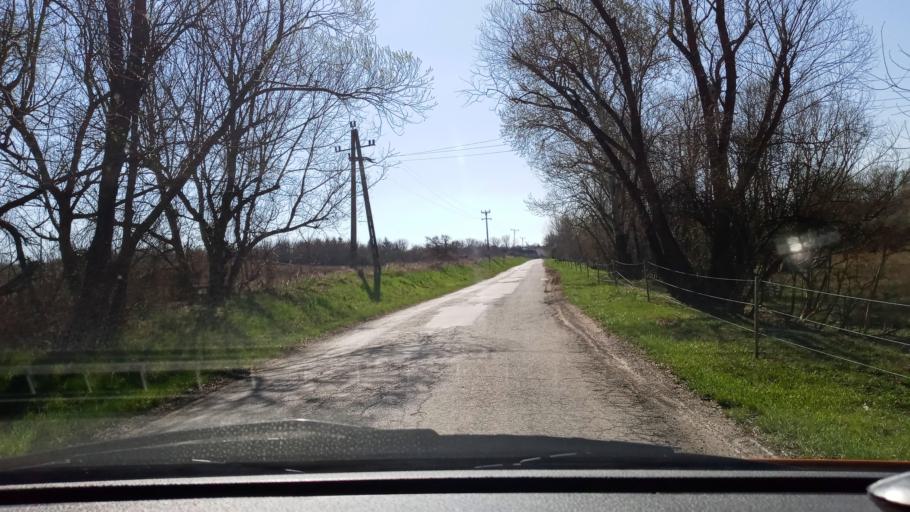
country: HU
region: Baranya
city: Kozarmisleny
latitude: 46.0664
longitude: 18.3702
